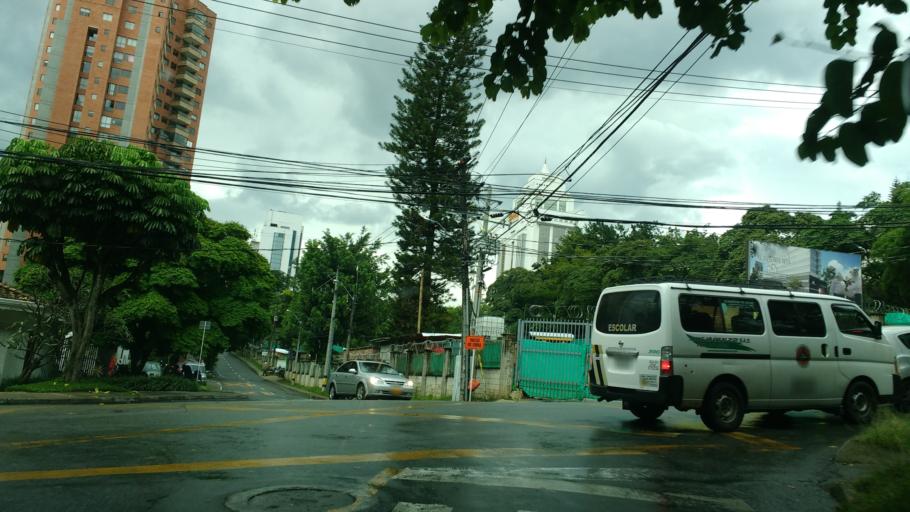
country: CO
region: Antioquia
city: Envigado
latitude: 6.1875
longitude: -75.5785
